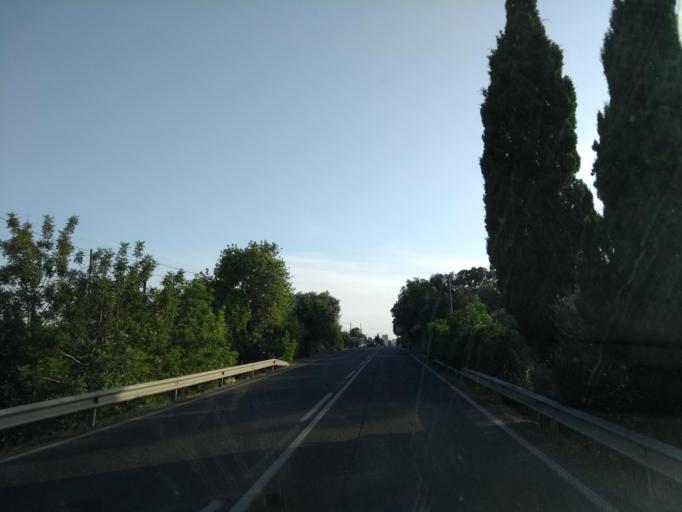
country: ES
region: Balearic Islands
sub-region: Illes Balears
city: Inca
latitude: 39.7313
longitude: 2.9325
